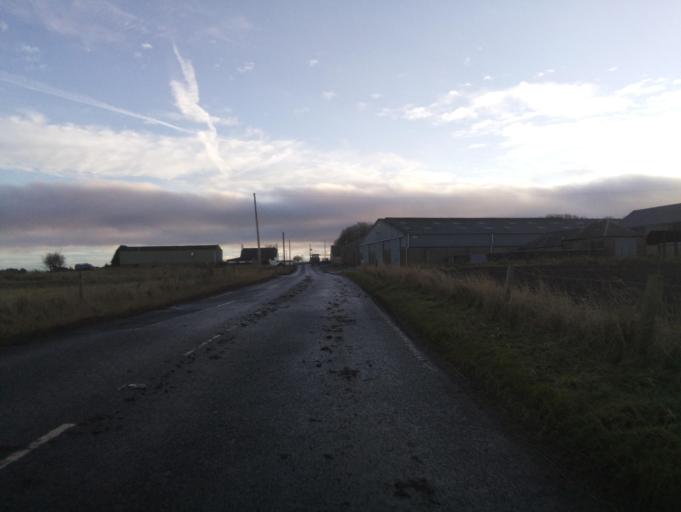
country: GB
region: Scotland
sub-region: Angus
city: Letham
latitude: 56.5697
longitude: -2.7779
